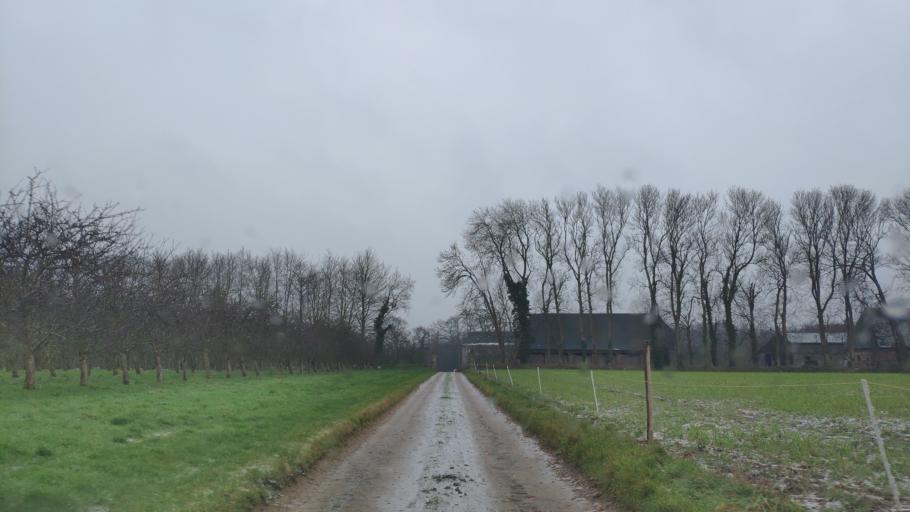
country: FR
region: Haute-Normandie
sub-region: Departement de la Seine-Maritime
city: Neville
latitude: 49.7929
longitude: 0.6999
